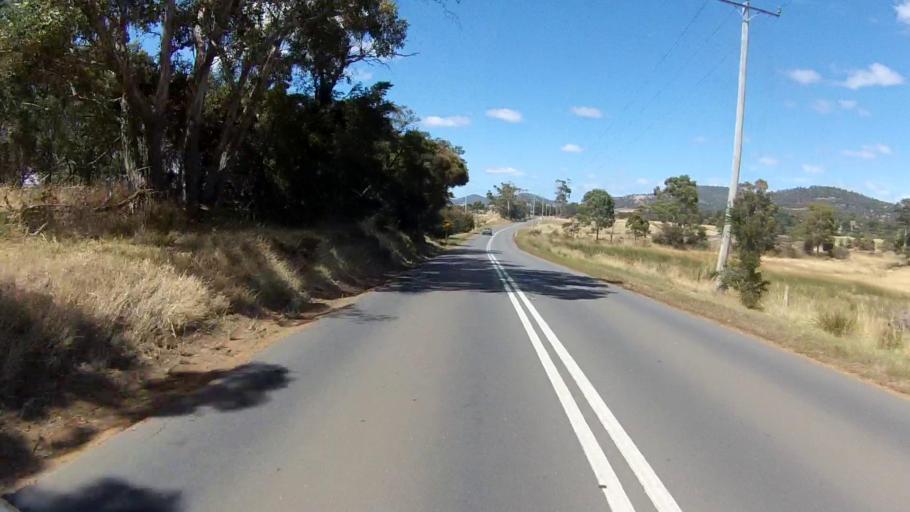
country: AU
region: Tasmania
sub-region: Clarence
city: Cambridge
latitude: -42.7660
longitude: 147.4155
